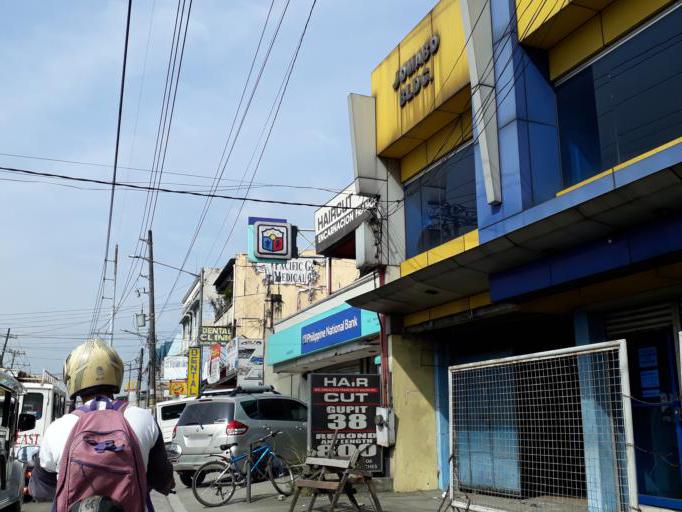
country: PH
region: Calabarzon
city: Bagong Pagasa
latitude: 14.6885
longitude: 121.0259
